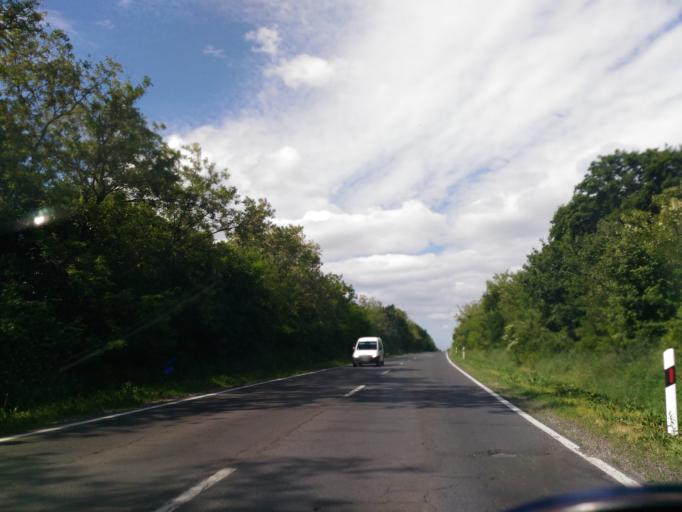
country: HU
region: Pest
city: Tarnok
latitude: 47.3474
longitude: 18.8481
